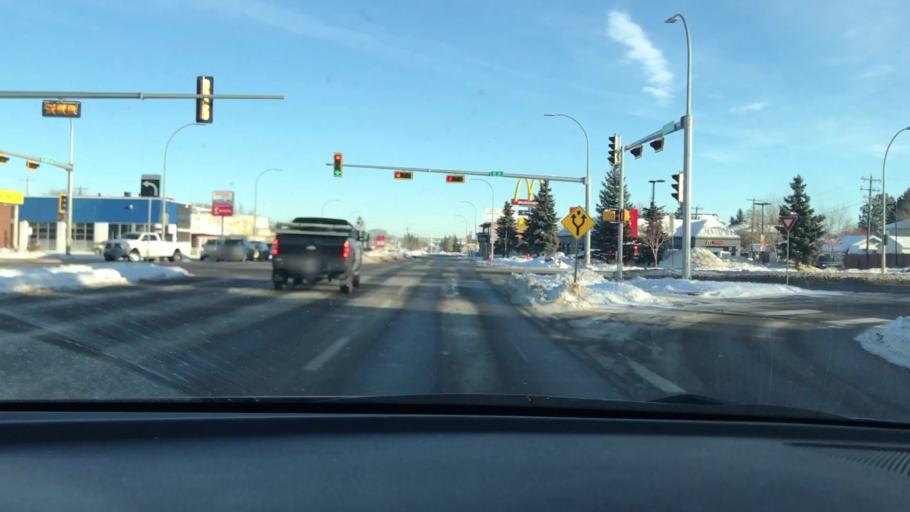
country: CA
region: Alberta
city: Edmonton
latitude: 53.5180
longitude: -113.4435
